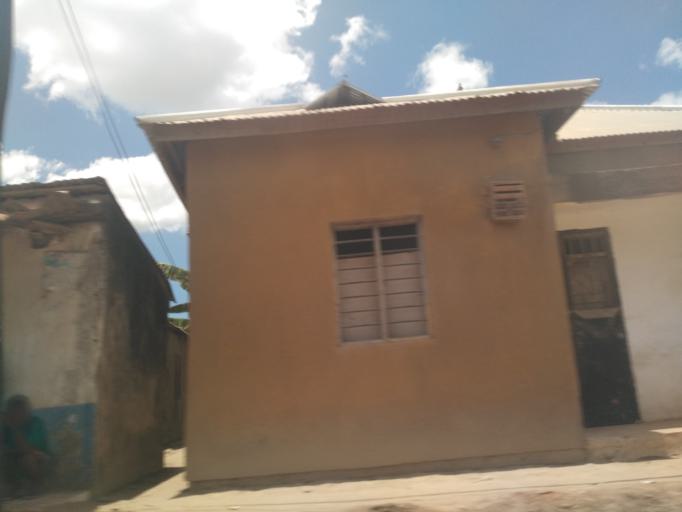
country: TZ
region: Dar es Salaam
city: Dar es Salaam
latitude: -6.8765
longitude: 39.2430
